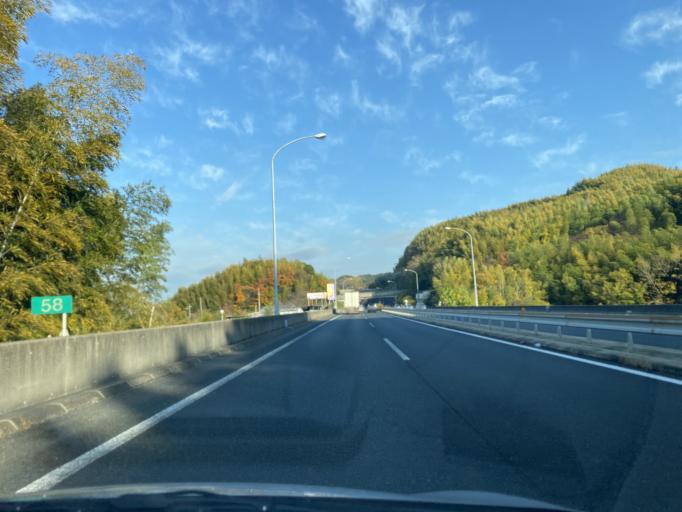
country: JP
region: Osaka
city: Kaizuka
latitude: 34.4002
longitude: 135.4129
